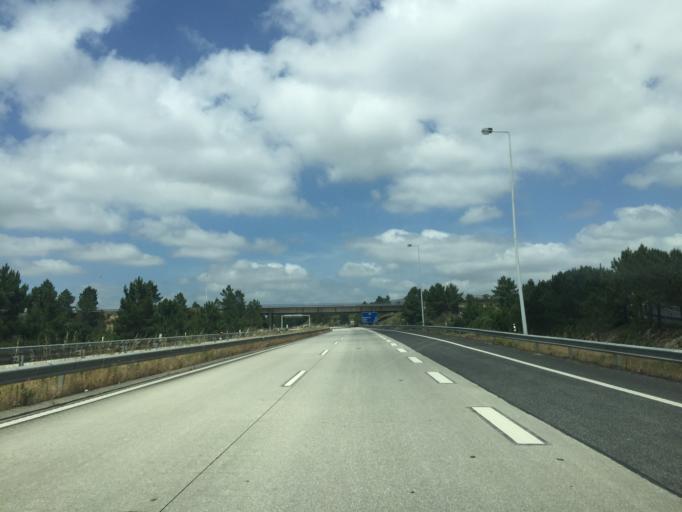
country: PT
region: Lisbon
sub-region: Torres Vedras
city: Torres Vedras
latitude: 39.1275
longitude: -9.2508
